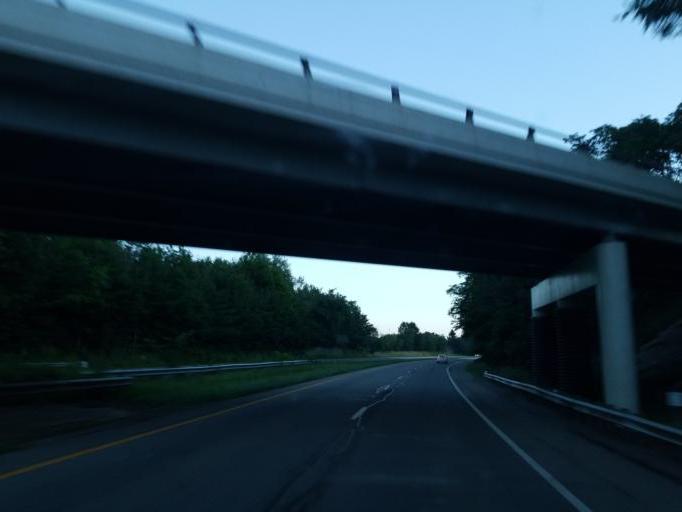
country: US
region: Ohio
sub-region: Summit County
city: Clinton
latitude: 40.9036
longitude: -81.6468
